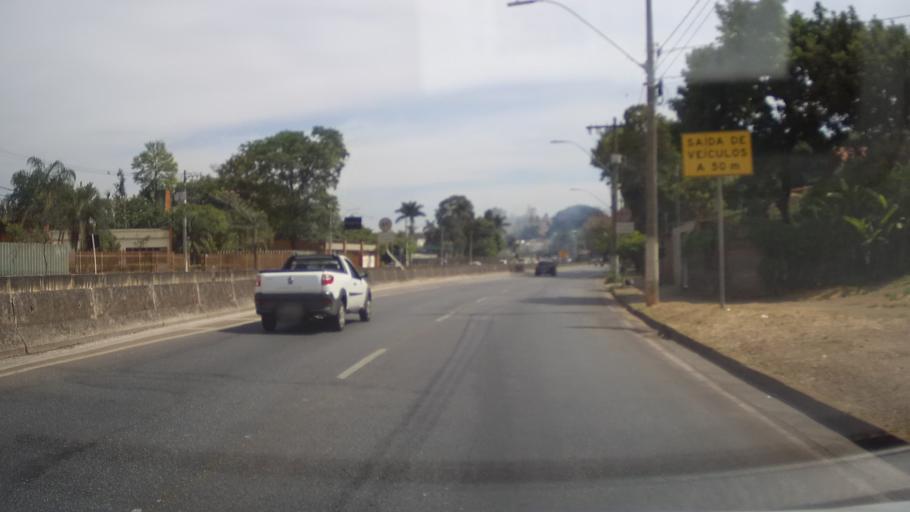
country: BR
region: Minas Gerais
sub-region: Belo Horizonte
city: Belo Horizonte
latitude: -19.9295
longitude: -43.9833
